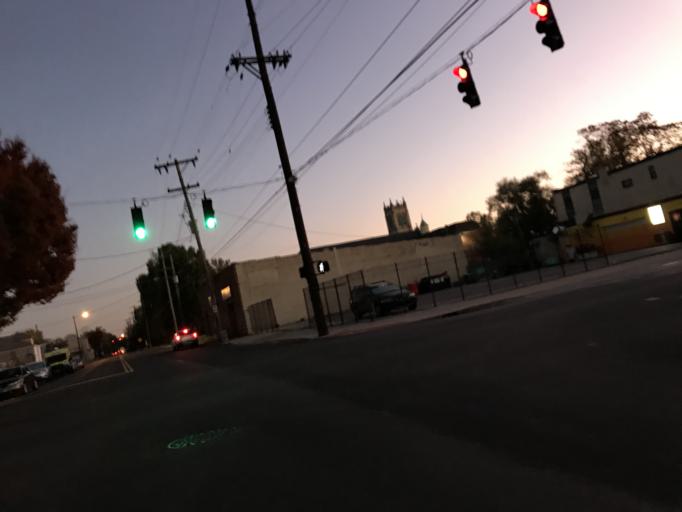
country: US
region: Kentucky
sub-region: Jefferson County
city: Louisville
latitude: 38.2354
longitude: -85.7651
